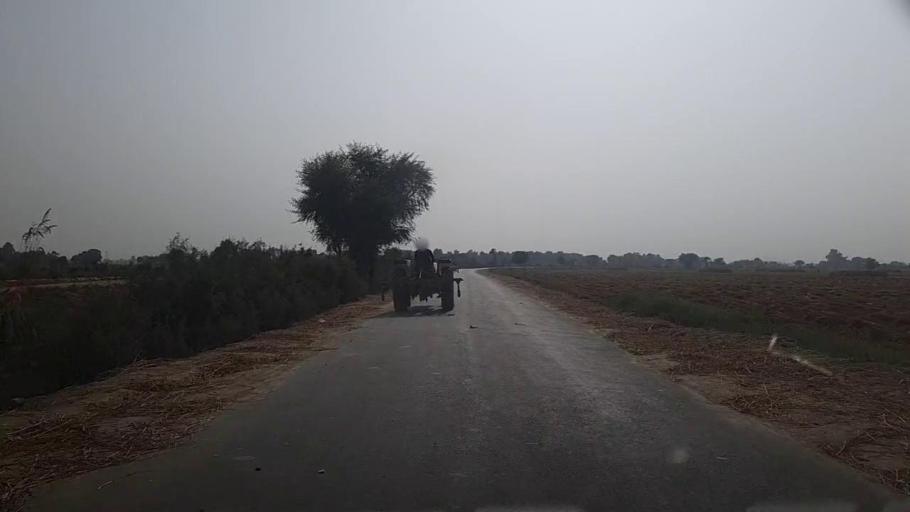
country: PK
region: Sindh
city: Kashmor
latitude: 28.4139
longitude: 69.5669
